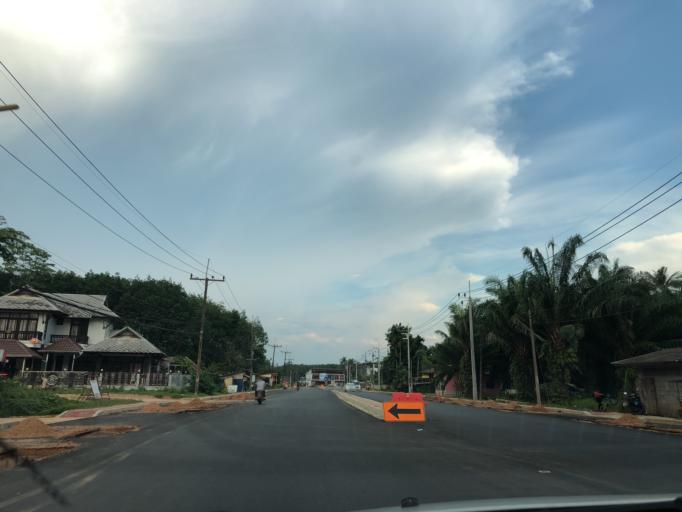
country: TH
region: Phangnga
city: Ban Ao Nang
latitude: 8.0705
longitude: 98.8382
